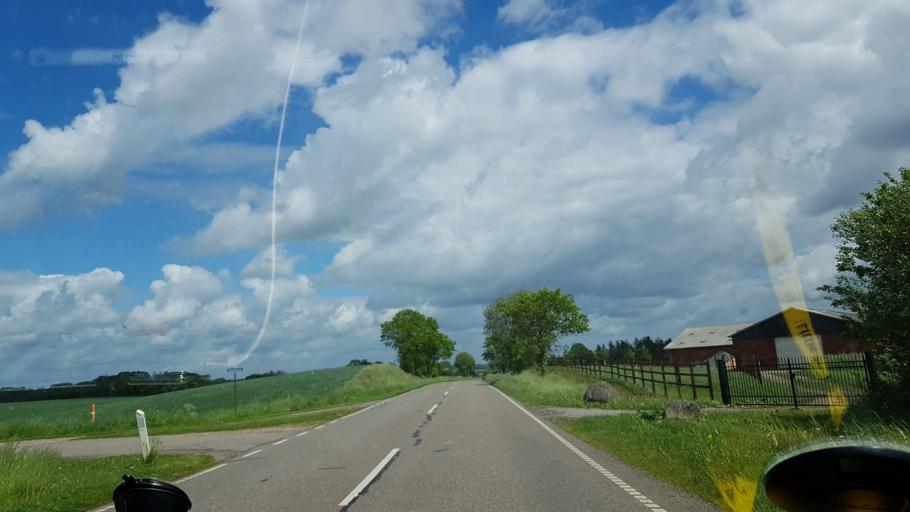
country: DK
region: South Denmark
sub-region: Kolding Kommune
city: Christiansfeld
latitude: 55.3376
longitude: 9.4588
